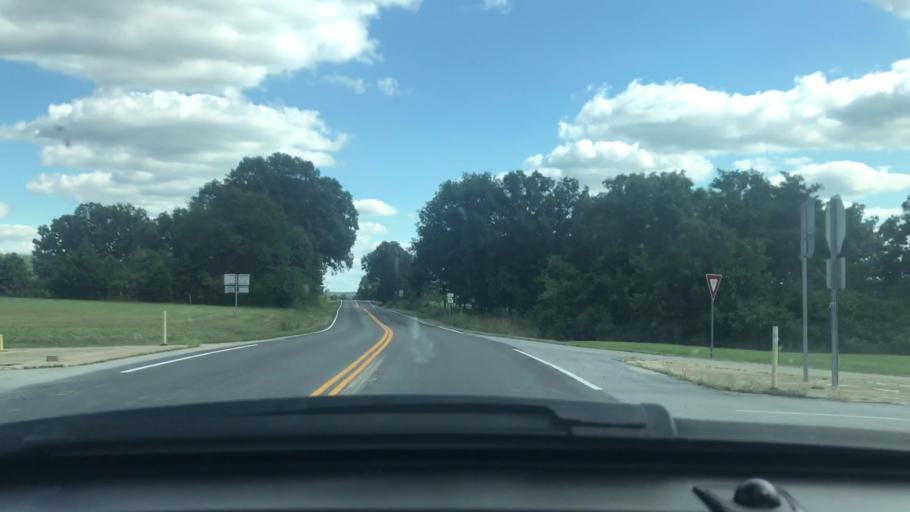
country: US
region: Missouri
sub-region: Wright County
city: Mountain Grove
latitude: 37.3004
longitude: -92.3127
